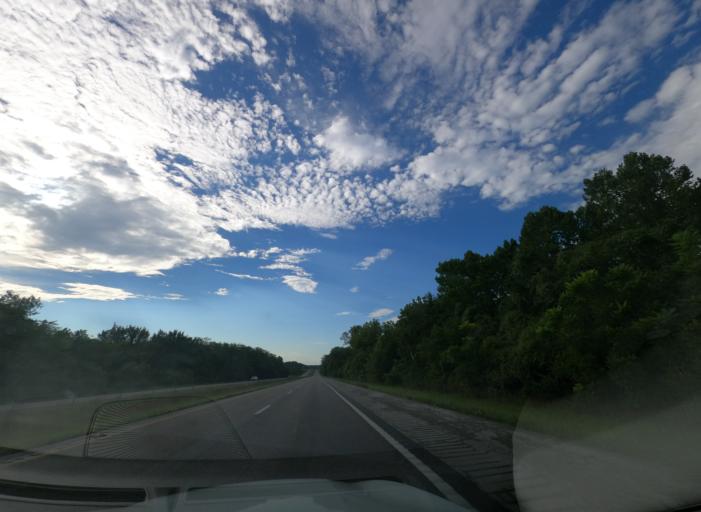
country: US
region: Missouri
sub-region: Jefferson County
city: Crystal City
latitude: 38.1343
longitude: -90.3211
